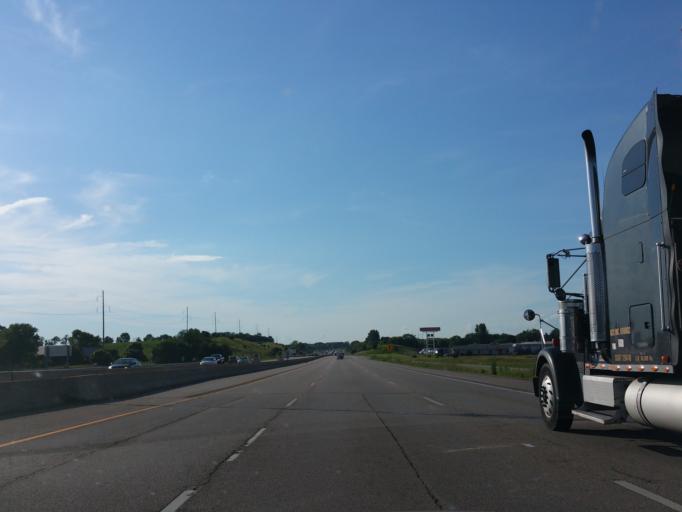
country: US
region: Wisconsin
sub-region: Dane County
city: Windsor
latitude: 43.1947
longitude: -89.3447
